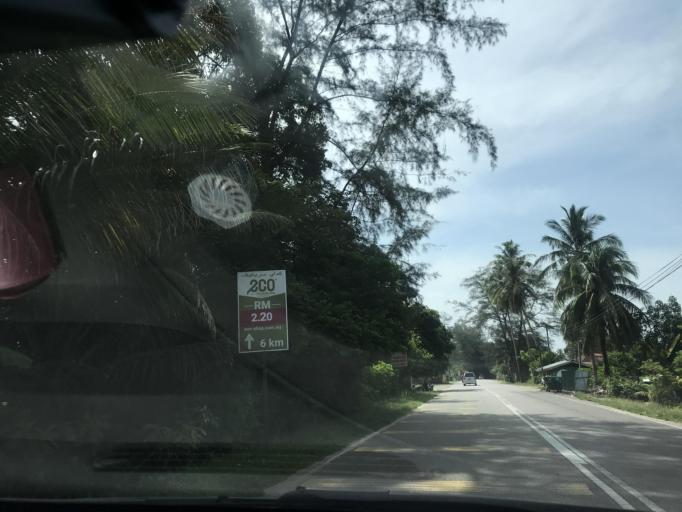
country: MY
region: Kelantan
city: Tumpat
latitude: 6.2153
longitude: 102.1256
